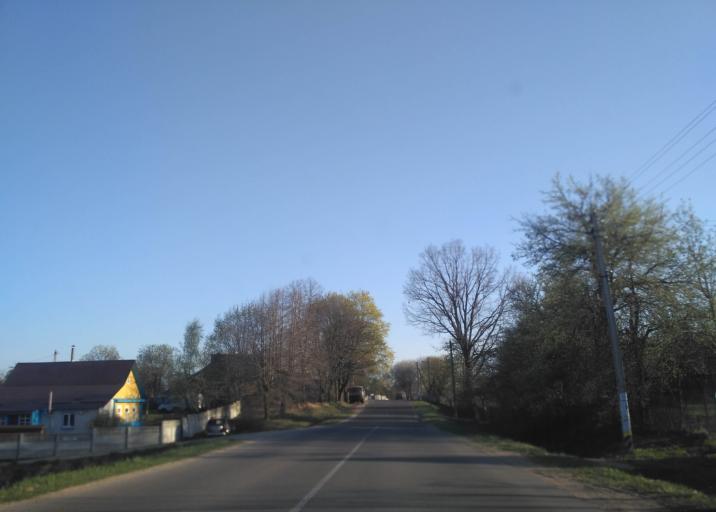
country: BY
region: Minsk
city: Pyatryshki
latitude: 54.1137
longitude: 27.1922
